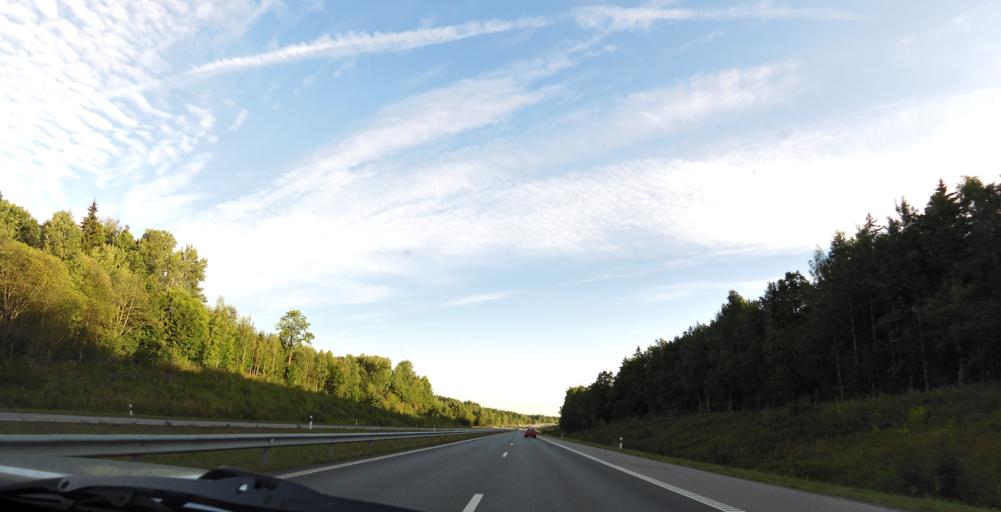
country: LT
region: Vilnius County
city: Ukmerge
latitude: 55.2141
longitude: 24.8171
